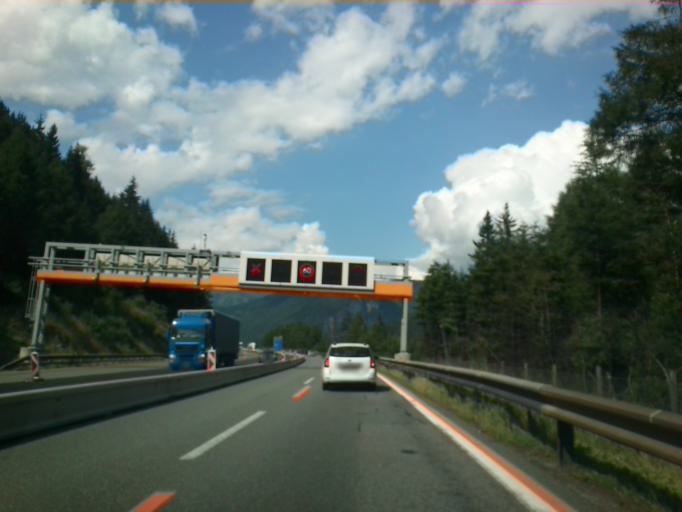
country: AT
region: Tyrol
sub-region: Politischer Bezirk Innsbruck Land
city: Gries am Brenner
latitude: 47.0448
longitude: 11.4799
